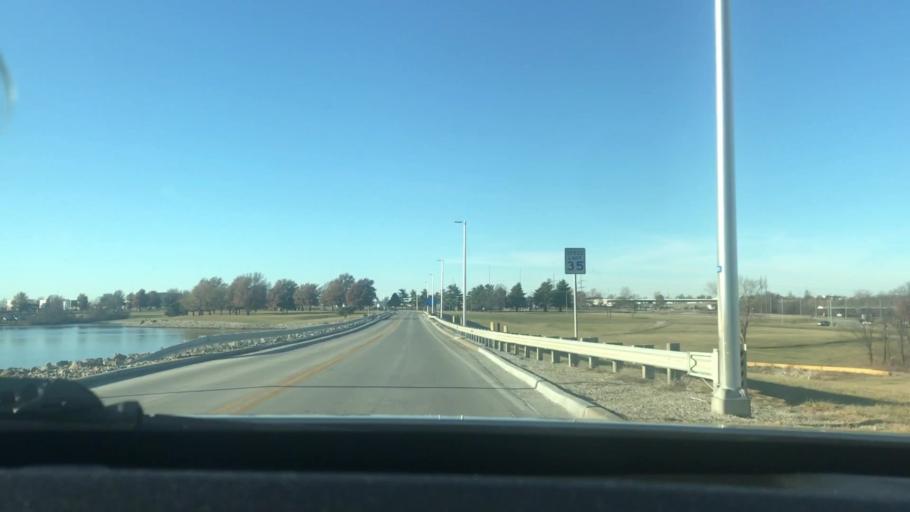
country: US
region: Missouri
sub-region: Platte County
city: Weatherby Lake
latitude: 39.3094
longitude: -94.7082
